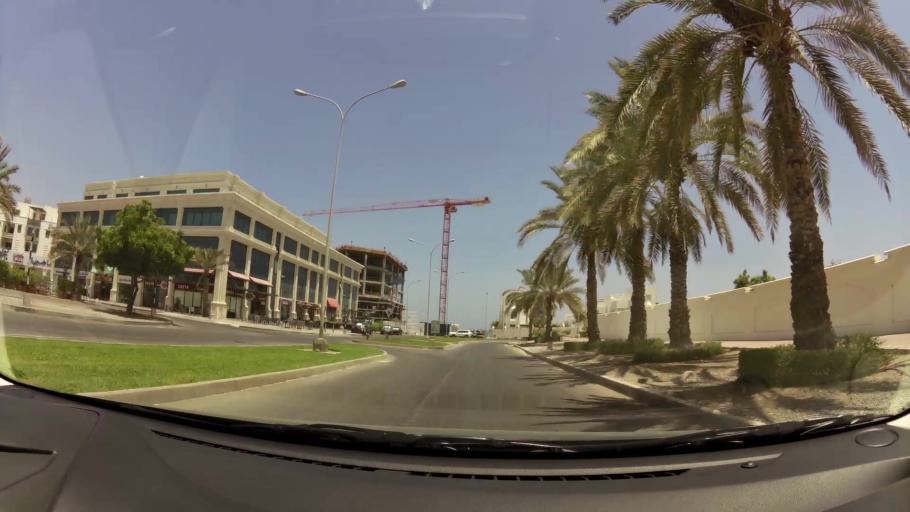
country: OM
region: Muhafazat Masqat
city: Bawshar
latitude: 23.6117
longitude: 58.4545
